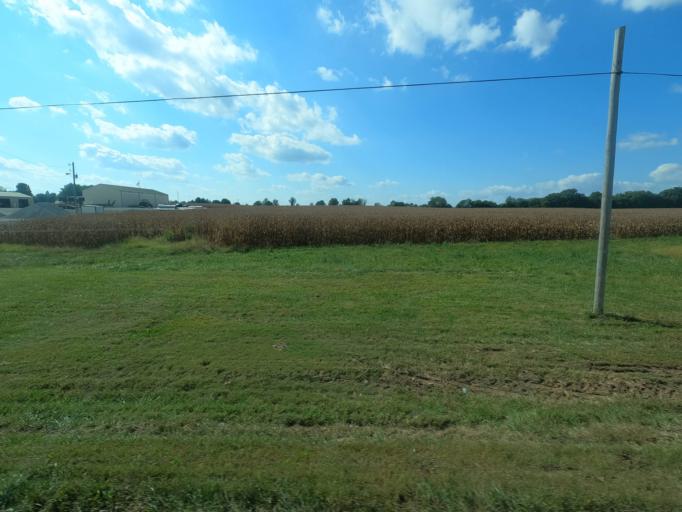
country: US
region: Illinois
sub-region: Massac County
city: Metropolis
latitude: 37.1777
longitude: -88.6767
